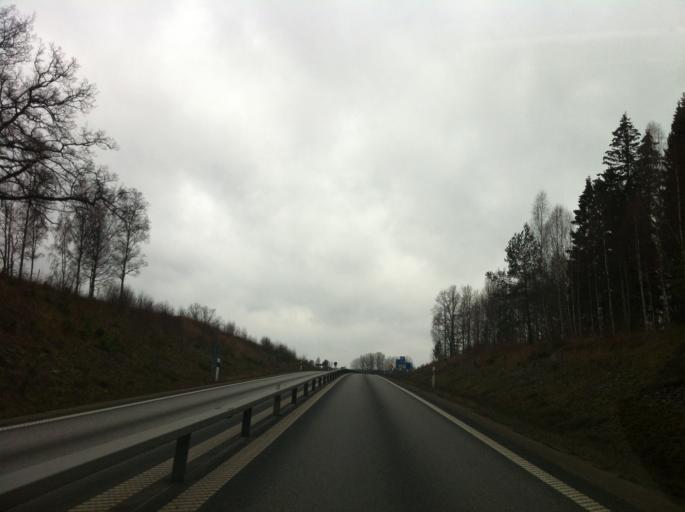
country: SE
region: Joenkoeping
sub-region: Vetlanda Kommun
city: Vetlanda
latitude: 57.4222
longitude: 15.1153
